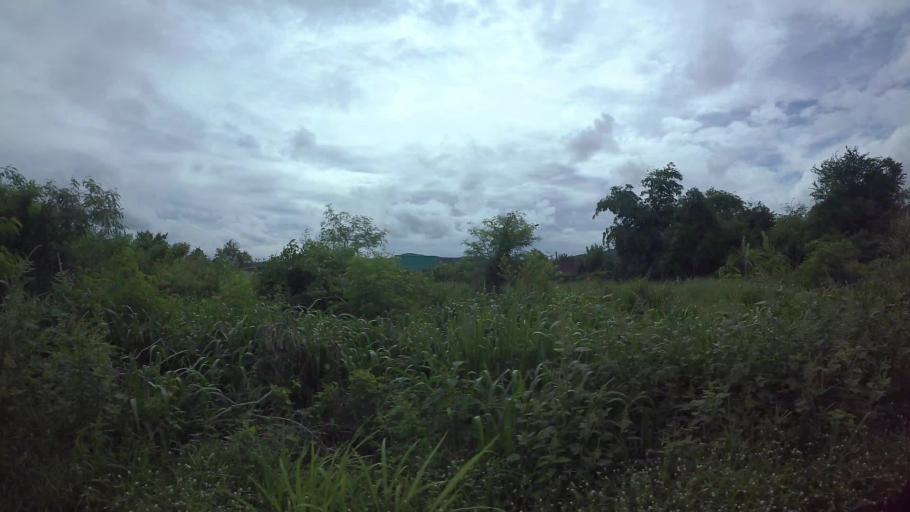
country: TH
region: Chon Buri
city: Sattahip
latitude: 12.7122
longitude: 100.8990
